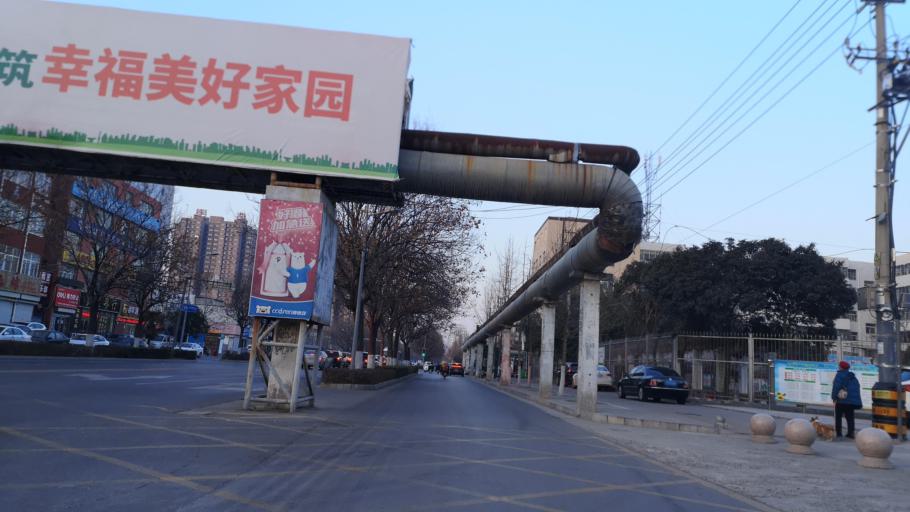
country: CN
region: Henan Sheng
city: Puyang
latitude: 35.7681
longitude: 115.0142
